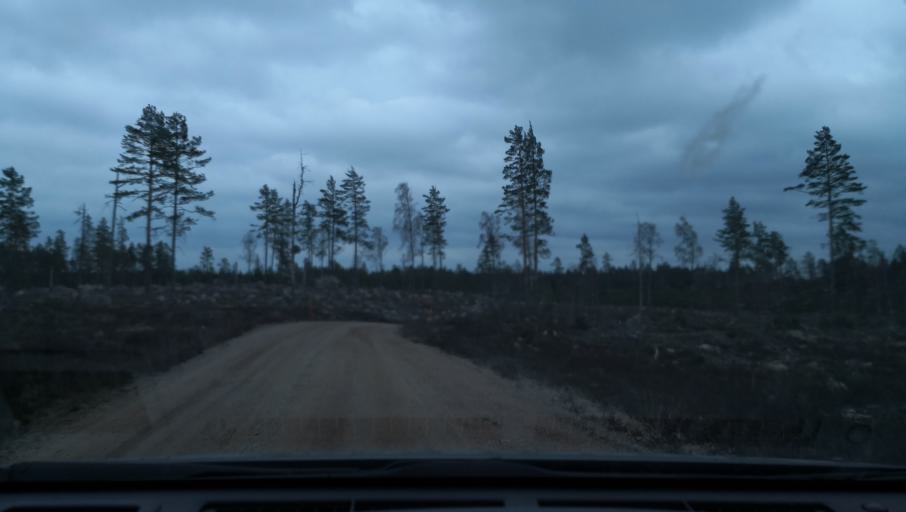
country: SE
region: OErebro
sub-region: Lindesbergs Kommun
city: Fellingsbro
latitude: 59.6002
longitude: 15.5799
